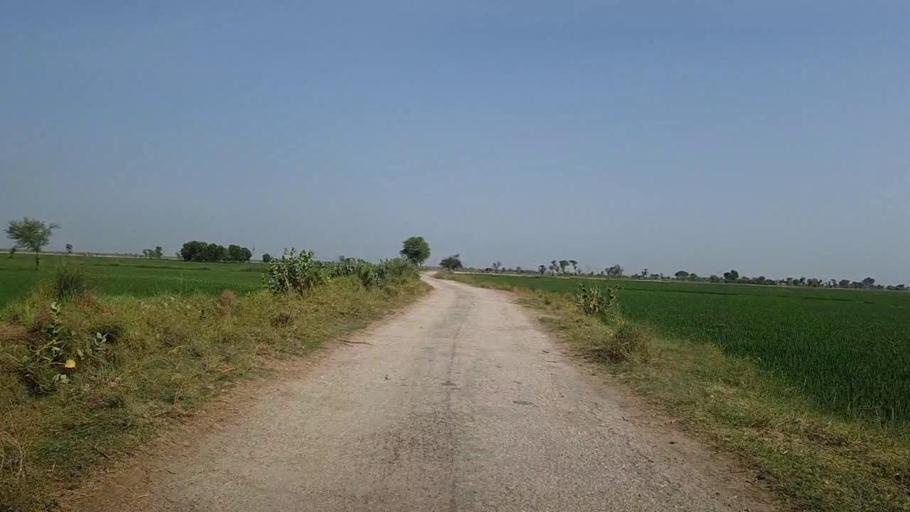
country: PK
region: Sindh
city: Sita Road
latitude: 27.1061
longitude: 67.8507
